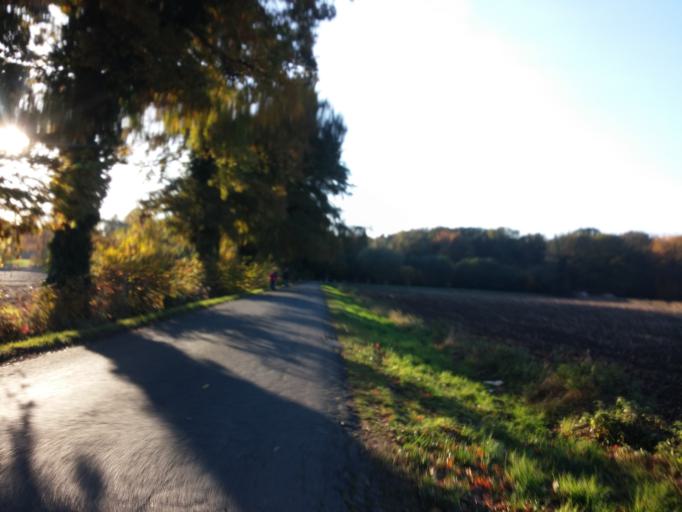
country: DE
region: North Rhine-Westphalia
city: Dorsten
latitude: 51.6364
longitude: 6.9822
